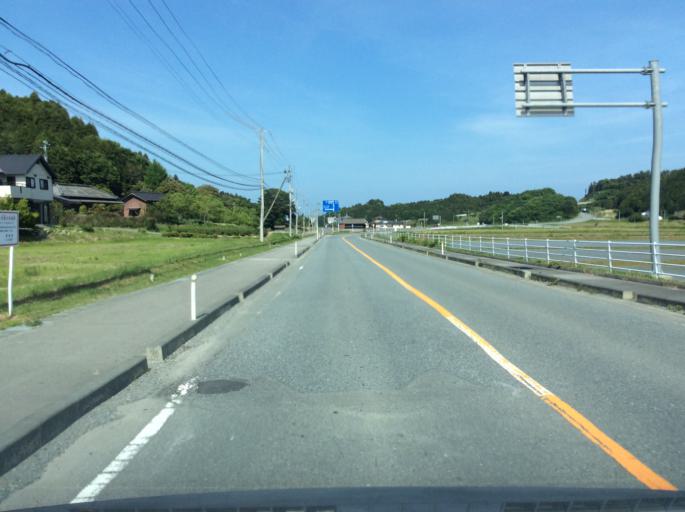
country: JP
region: Fukushima
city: Iwaki
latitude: 37.1400
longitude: 140.9806
